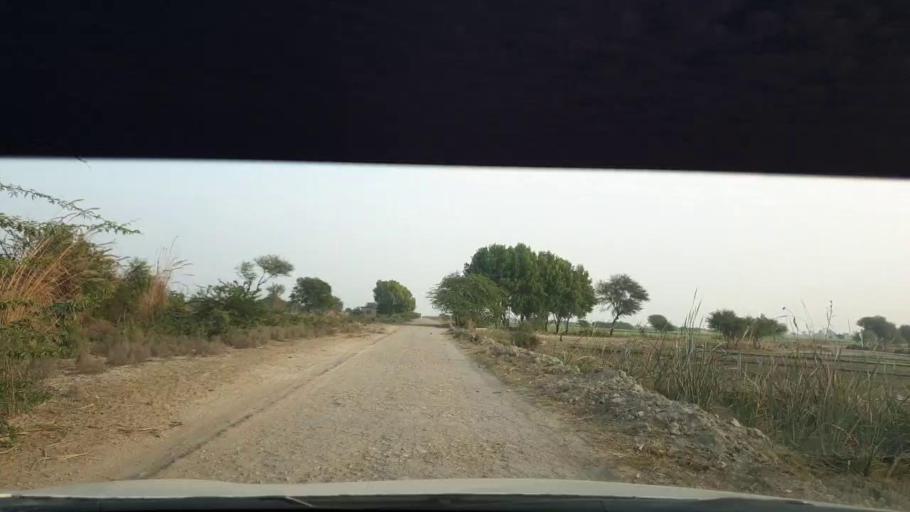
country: PK
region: Sindh
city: Berani
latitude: 25.7276
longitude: 68.9722
